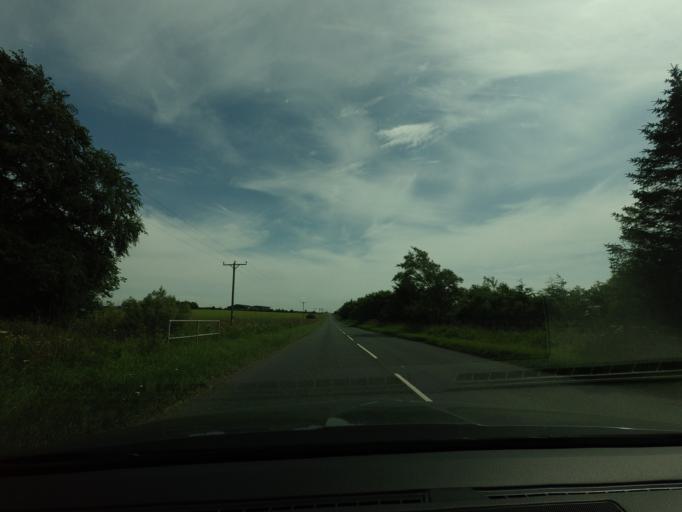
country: GB
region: Scotland
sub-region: Aberdeenshire
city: Peterhead
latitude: 57.5076
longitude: -1.8913
